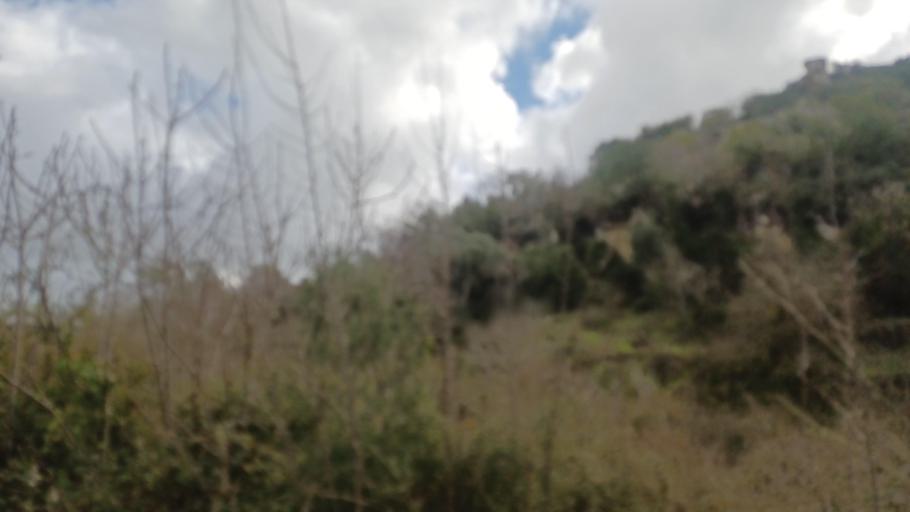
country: CY
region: Pafos
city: Pegeia
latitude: 34.9499
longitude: 32.4240
